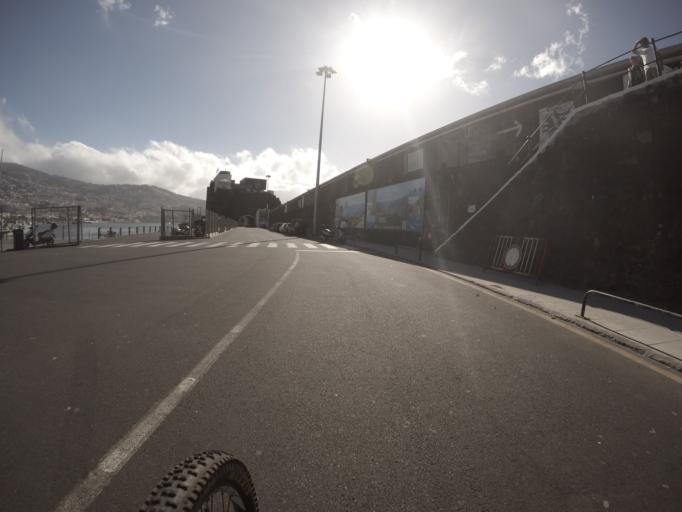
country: PT
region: Madeira
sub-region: Funchal
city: Funchal
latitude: 32.6412
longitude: -16.9172
